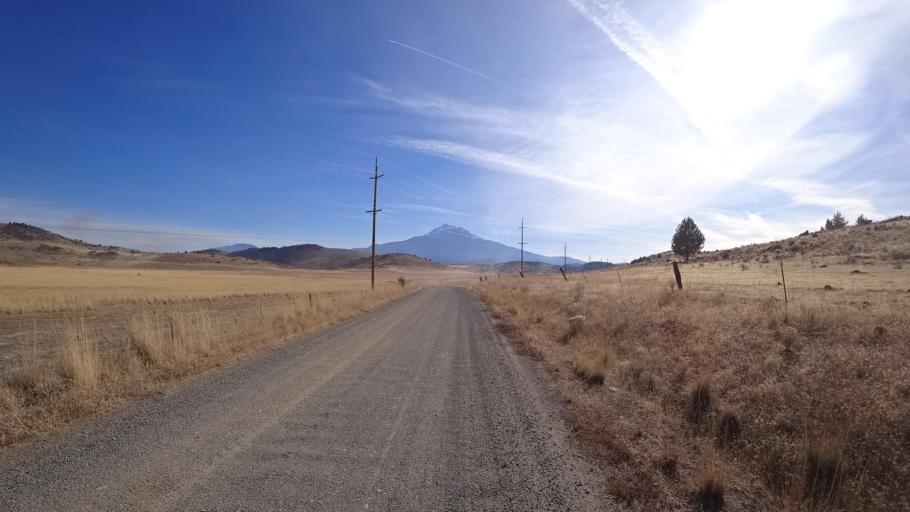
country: US
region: California
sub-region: Siskiyou County
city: Weed
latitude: 41.5118
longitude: -122.4678
